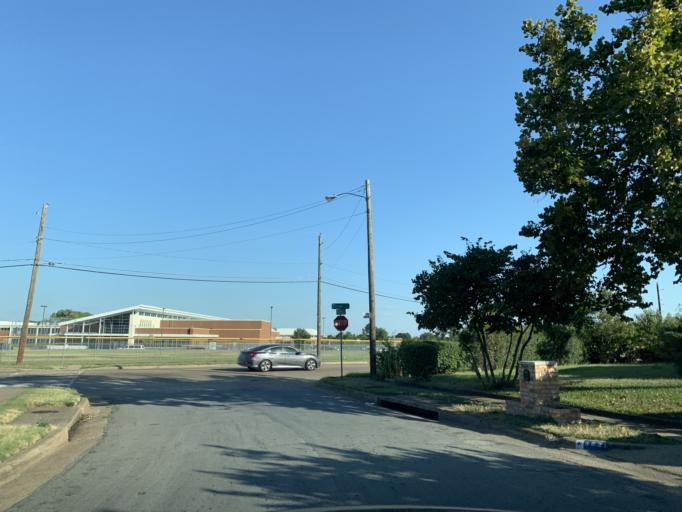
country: US
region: Texas
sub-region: Dallas County
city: Hutchins
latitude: 32.6628
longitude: -96.7602
